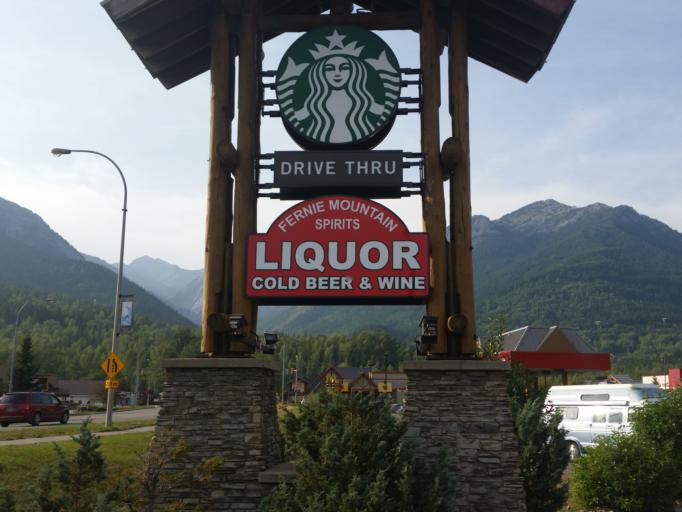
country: CA
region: British Columbia
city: Fernie
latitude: 49.5148
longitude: -115.0586
